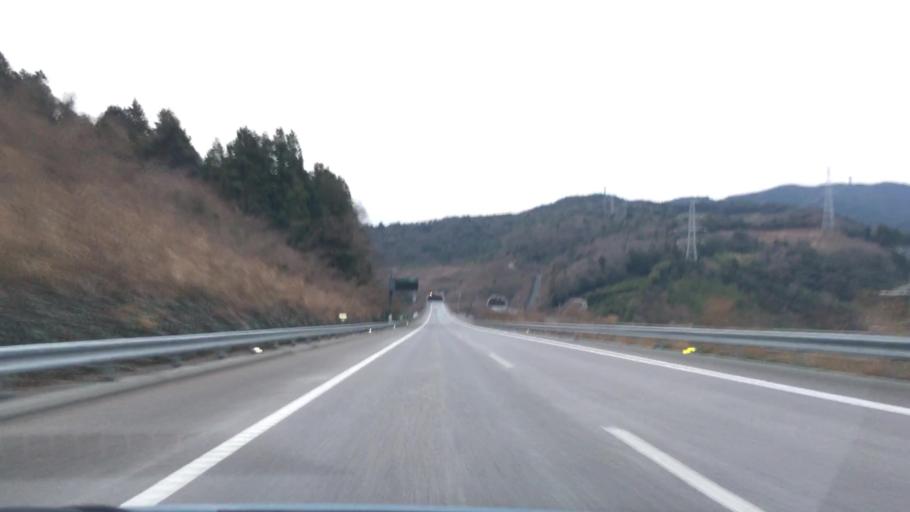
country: JP
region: Aichi
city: Shinshiro
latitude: 34.8582
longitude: 137.6246
